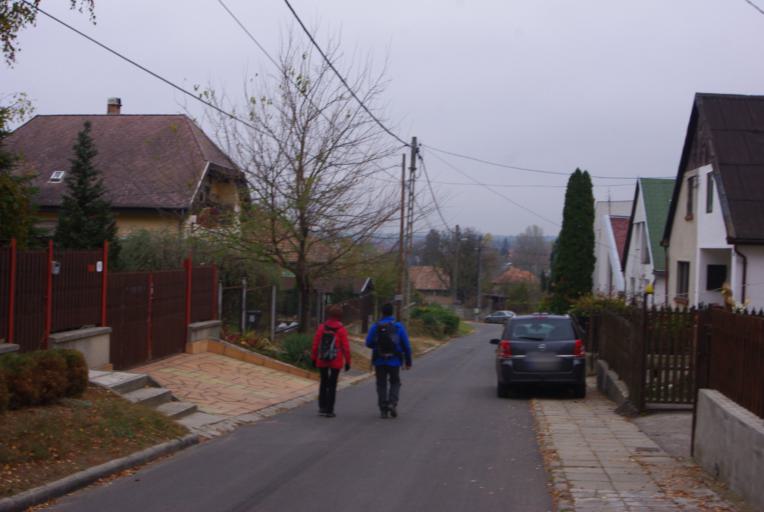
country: HU
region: Pest
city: Isaszeg
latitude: 47.5256
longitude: 19.4006
